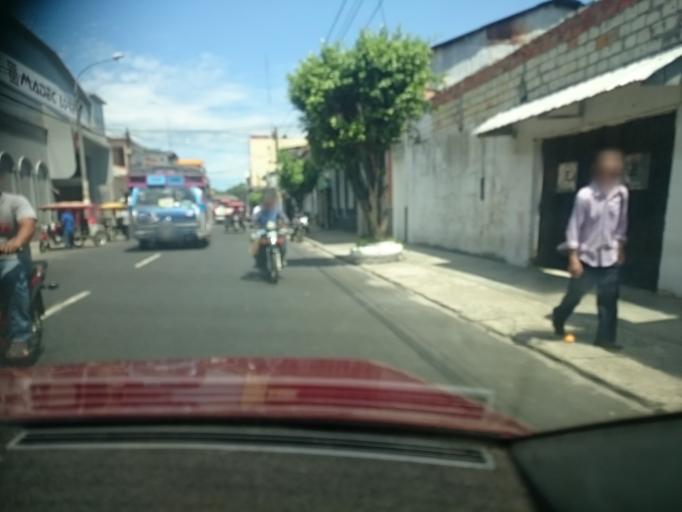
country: PE
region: Loreto
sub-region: Provincia de Maynas
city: Iquitos
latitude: -3.7522
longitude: -73.2478
